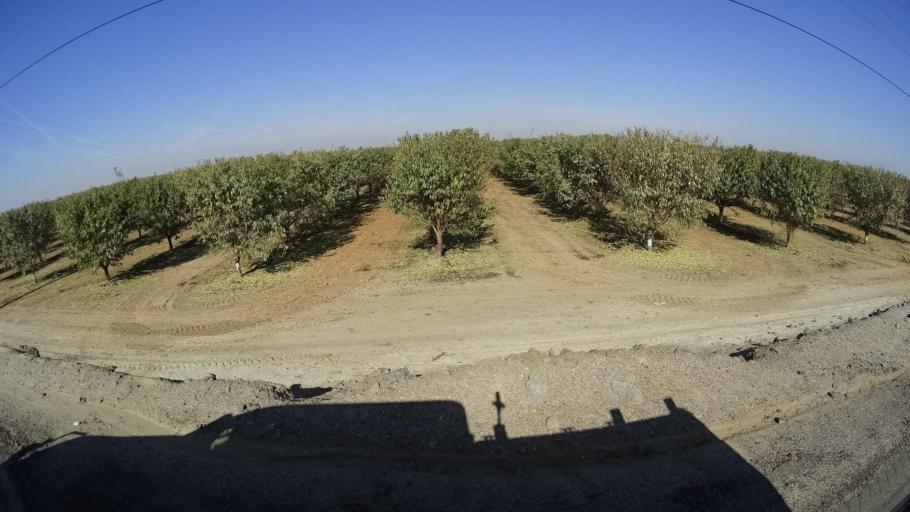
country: US
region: California
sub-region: Kern County
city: McFarland
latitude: 35.7034
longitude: -119.1937
